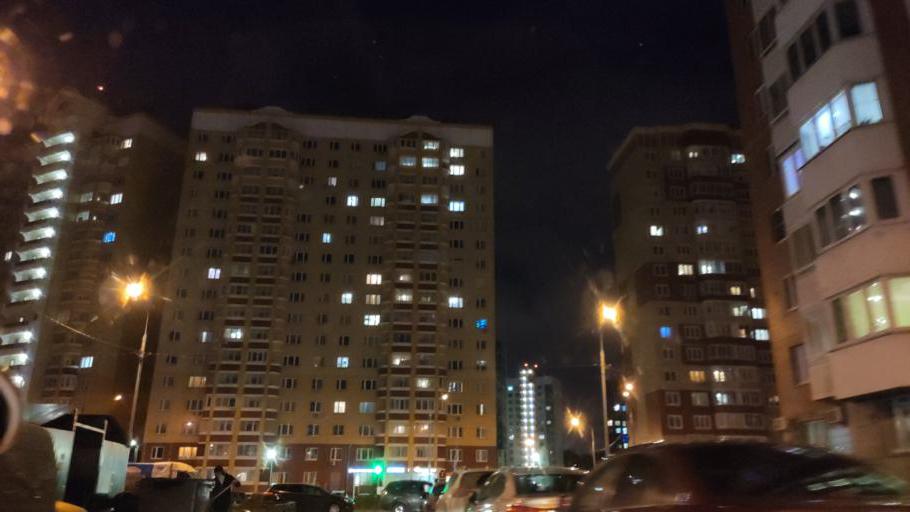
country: RU
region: Moscow
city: Annino
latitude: 55.5312
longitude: 37.6156
